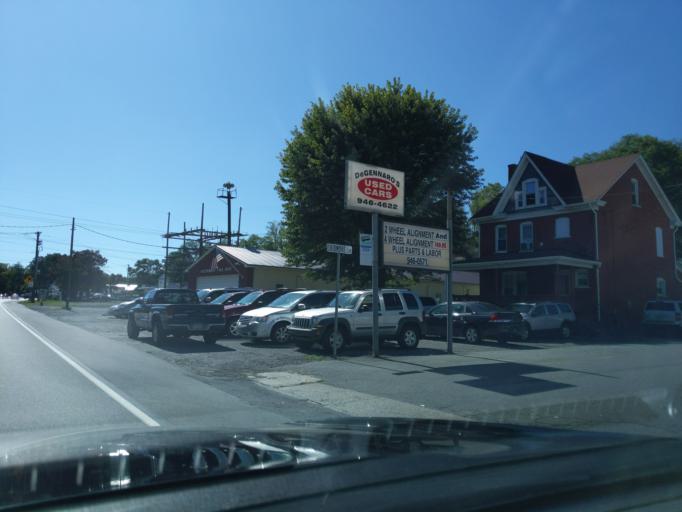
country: US
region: Pennsylvania
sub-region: Blair County
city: Greenwood
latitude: 40.5326
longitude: -78.3604
